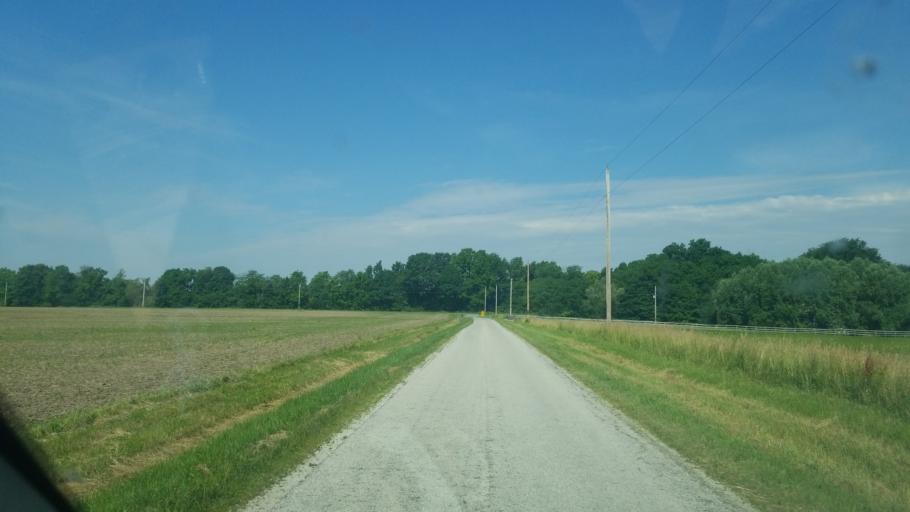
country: US
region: Ohio
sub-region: Wyandot County
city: Upper Sandusky
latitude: 40.9239
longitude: -83.2401
